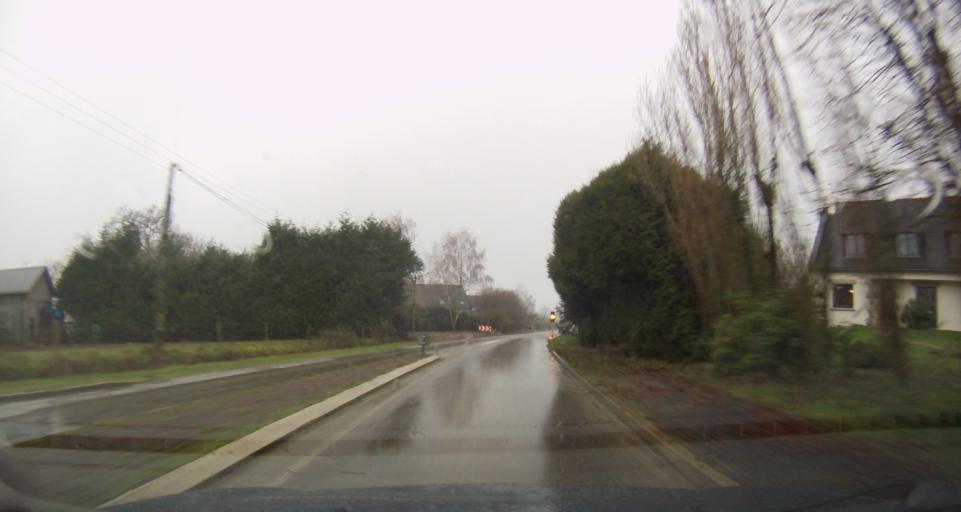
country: FR
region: Brittany
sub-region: Departement d'Ille-et-Vilaine
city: Chanteloup
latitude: 47.9647
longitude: -1.6218
